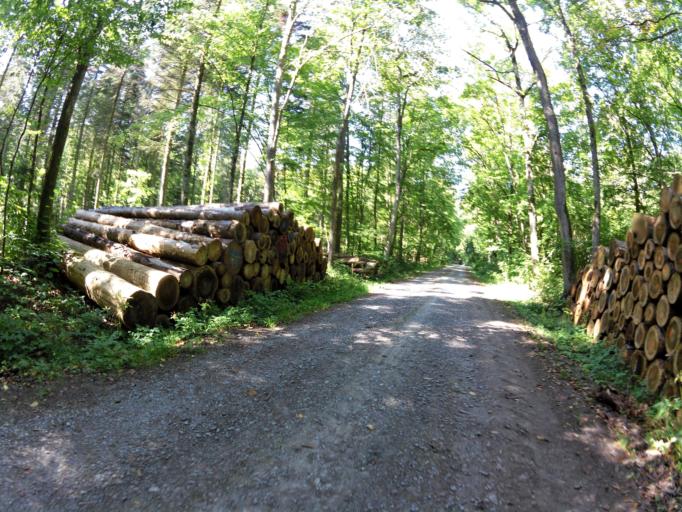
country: DE
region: Bavaria
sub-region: Regierungsbezirk Unterfranken
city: Kleinrinderfeld
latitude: 49.6959
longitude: 9.8089
